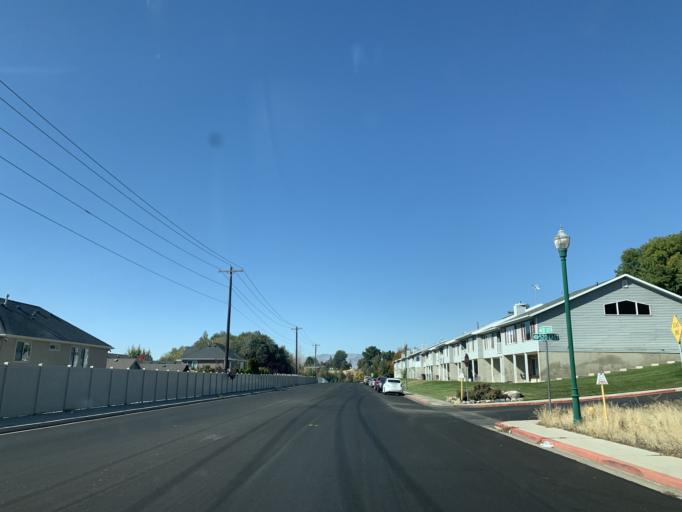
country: US
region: Utah
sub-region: Utah County
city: Provo
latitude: 40.2607
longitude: -111.6823
